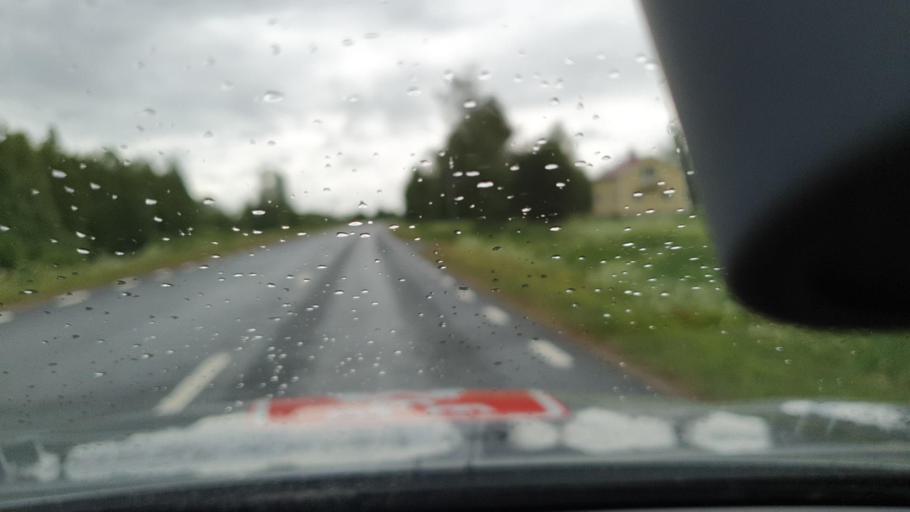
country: FI
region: Lapland
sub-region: Kemi-Tornio
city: Tornio
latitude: 66.0042
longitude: 24.0186
